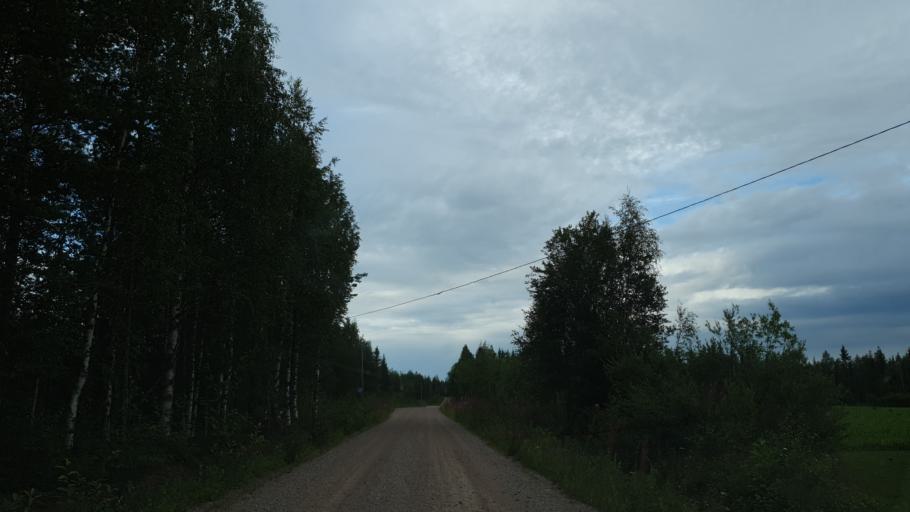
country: FI
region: Kainuu
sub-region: Kehys-Kainuu
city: Suomussalmi
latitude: 64.4453
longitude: 28.9672
